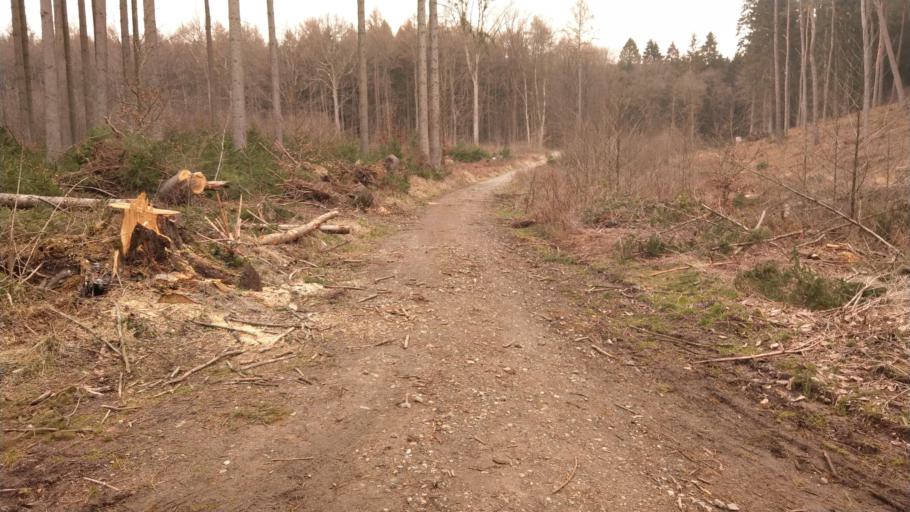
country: DE
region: North Rhine-Westphalia
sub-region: Regierungsbezirk Koln
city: Aachen
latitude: 50.7247
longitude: 6.0682
